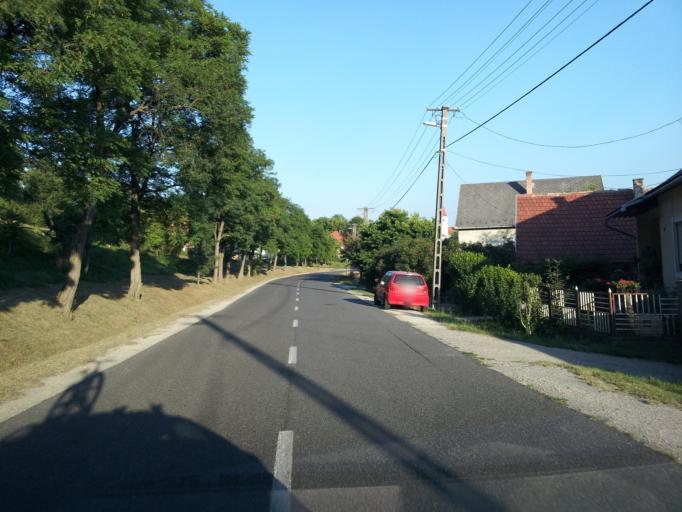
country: HU
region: Fejer
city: Many
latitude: 47.5223
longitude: 18.6121
